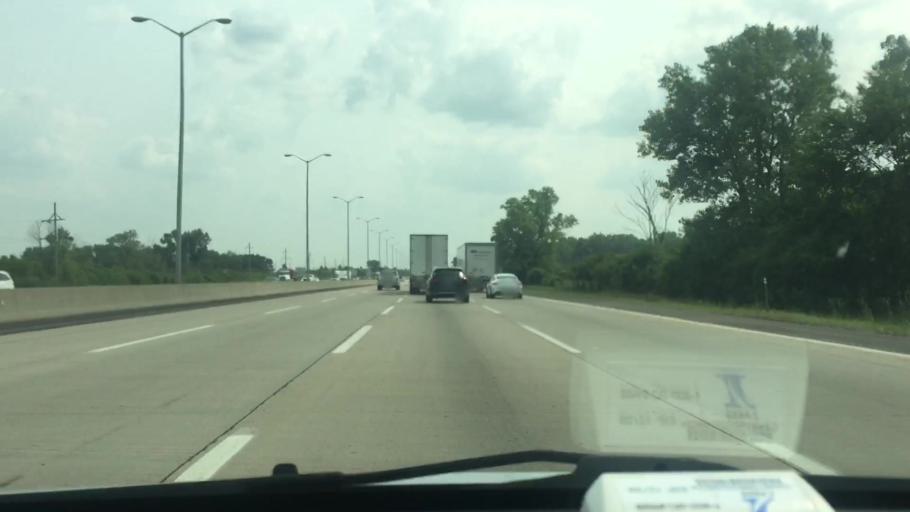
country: US
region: Illinois
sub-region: Lake County
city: Green Oaks
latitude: 42.3063
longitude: -87.9042
